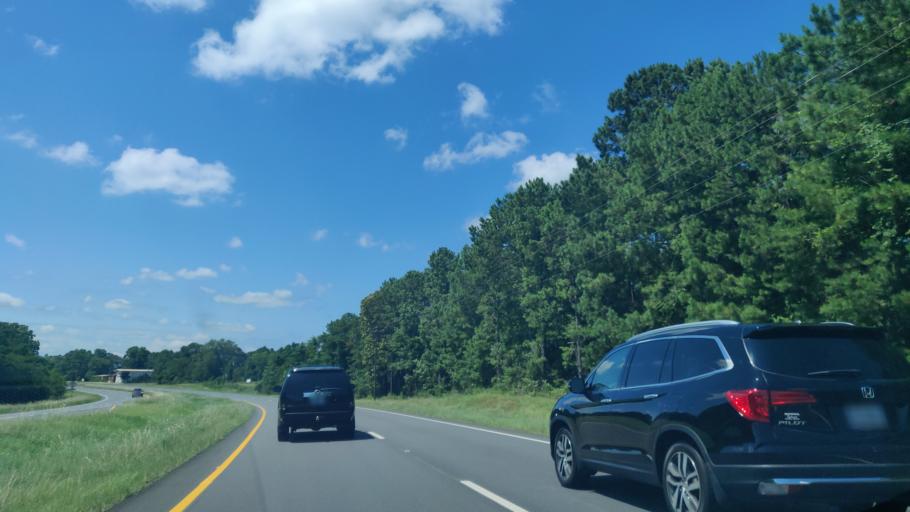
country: US
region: Georgia
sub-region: Stewart County
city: Richland
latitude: 32.1755
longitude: -84.7068
